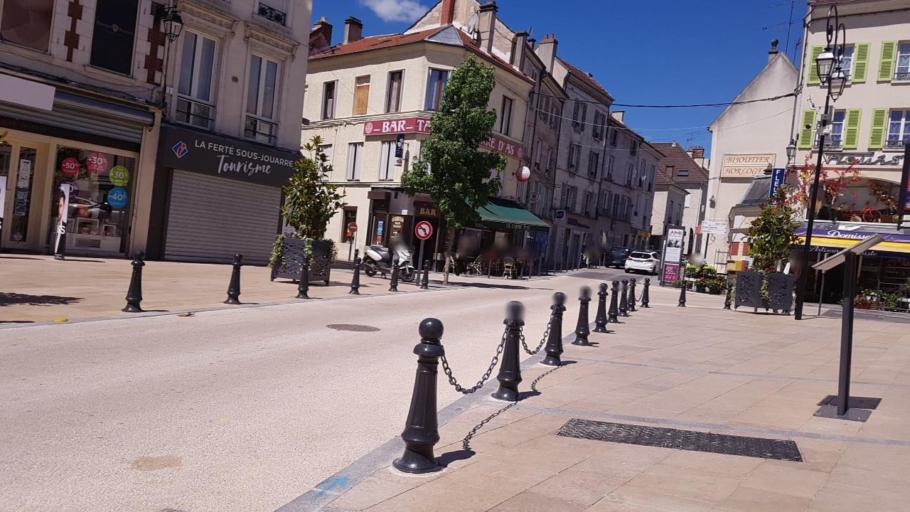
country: FR
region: Ile-de-France
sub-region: Departement de Seine-et-Marne
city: La Ferte-sous-Jouarre
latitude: 48.9498
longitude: 3.1293
